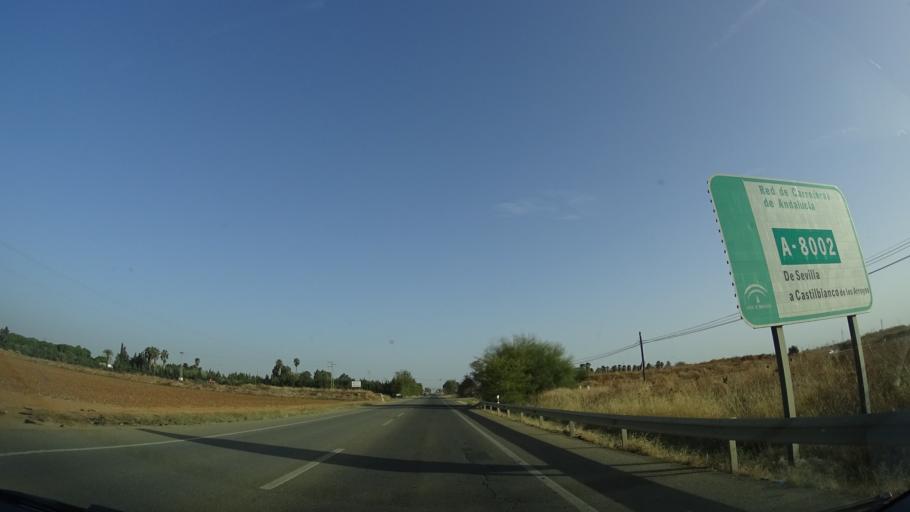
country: ES
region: Andalusia
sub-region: Provincia de Sevilla
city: La Algaba
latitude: 37.4387
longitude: -5.9788
